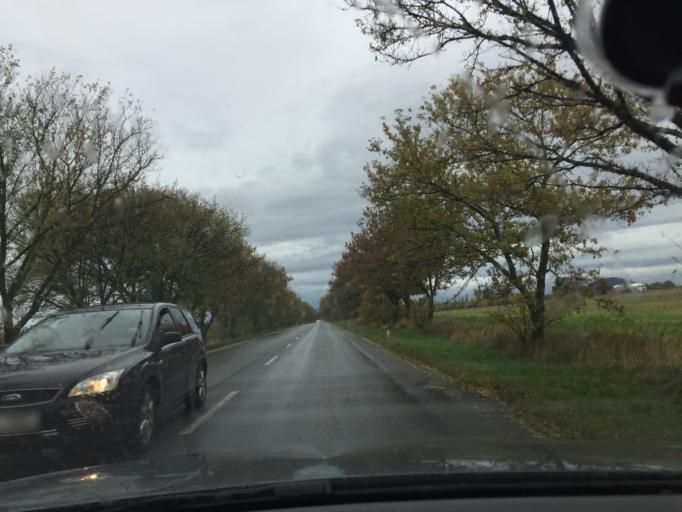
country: CZ
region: Central Bohemia
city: Nelahozeves
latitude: 50.3296
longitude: 14.2882
